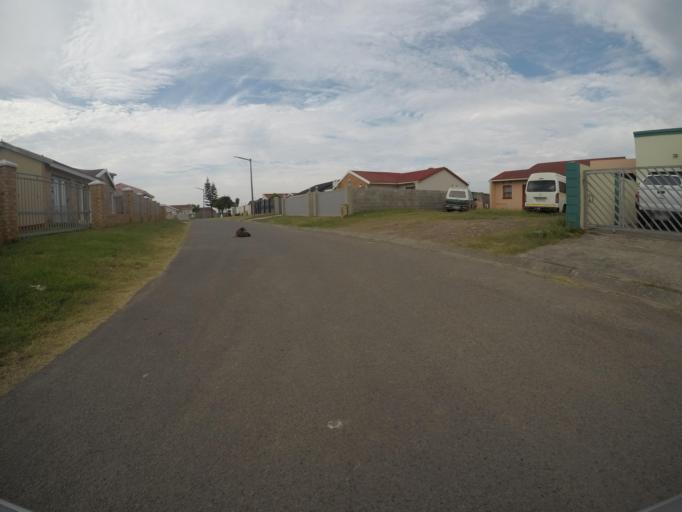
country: ZA
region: Eastern Cape
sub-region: Buffalo City Metropolitan Municipality
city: East London
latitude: -32.9768
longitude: 27.8582
